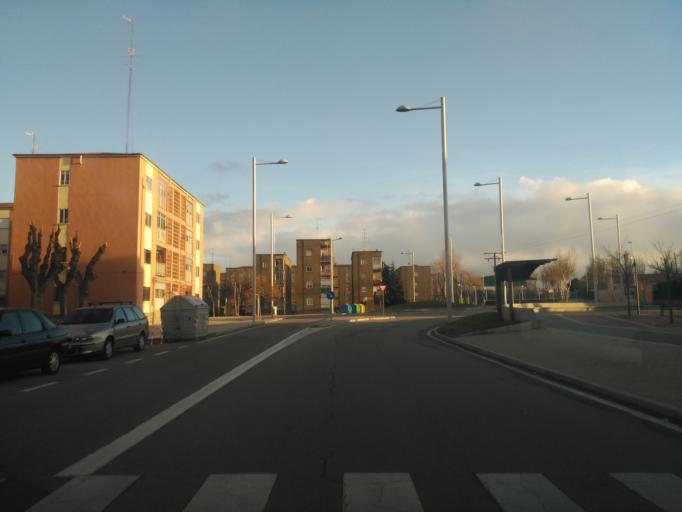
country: ES
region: Castille and Leon
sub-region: Provincia de Salamanca
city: Carbajosa de la Sagrada
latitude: 40.9481
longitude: -5.6615
